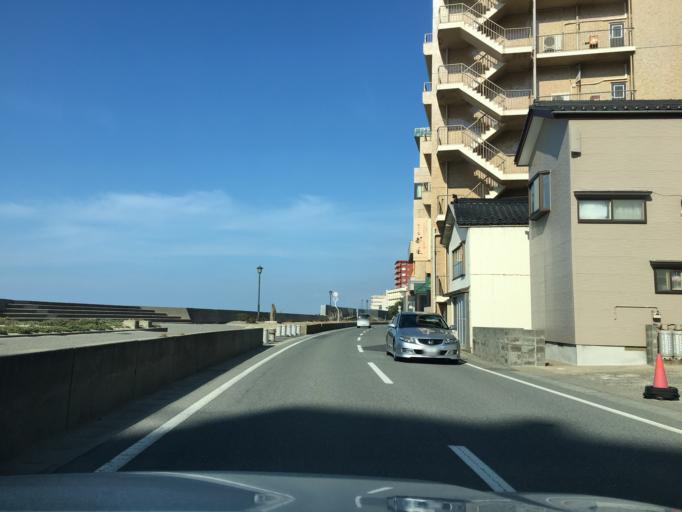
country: JP
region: Yamagata
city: Tsuruoka
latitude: 38.7782
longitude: 139.7496
